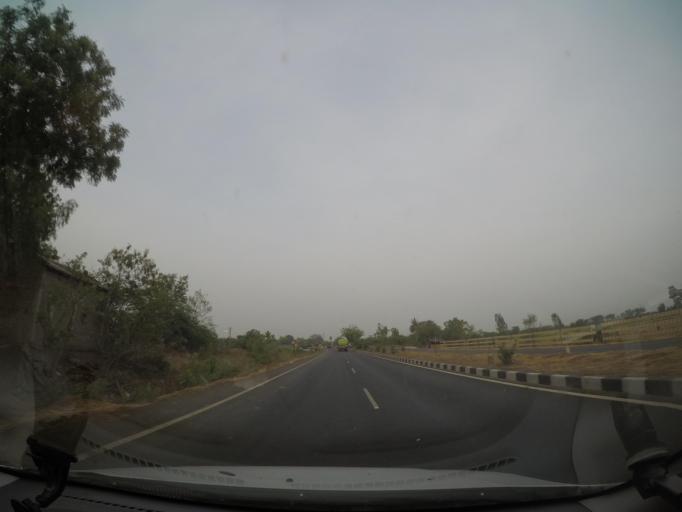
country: IN
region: Andhra Pradesh
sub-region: Krishna
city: Gannavaram
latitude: 16.6172
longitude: 80.9259
